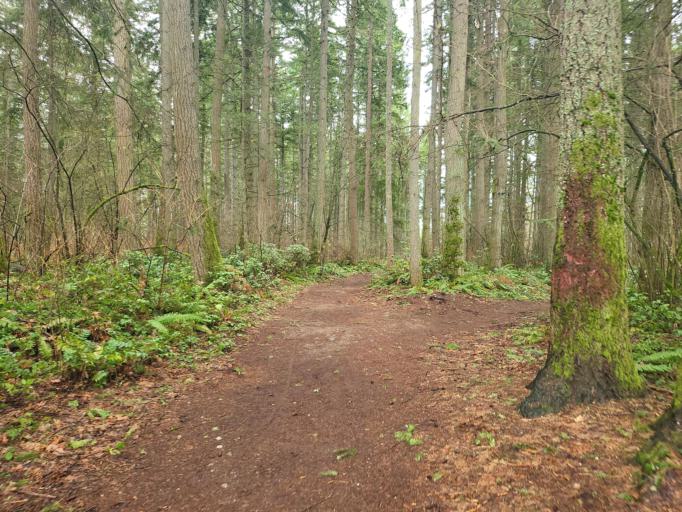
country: US
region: Washington
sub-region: King County
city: East Renton Highlands
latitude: 47.4810
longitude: -122.1455
